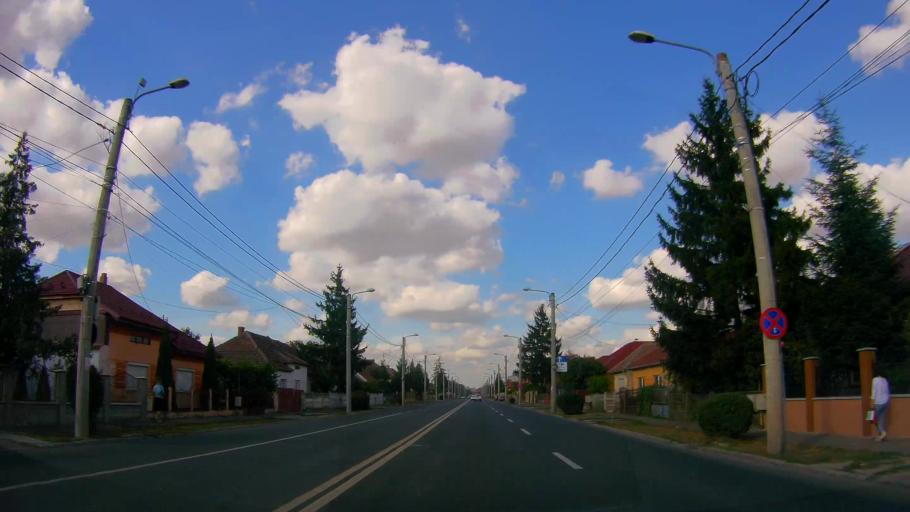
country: RO
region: Satu Mare
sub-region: Municipiul Satu Mare
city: Satu Mare
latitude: 47.7634
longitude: 22.8835
